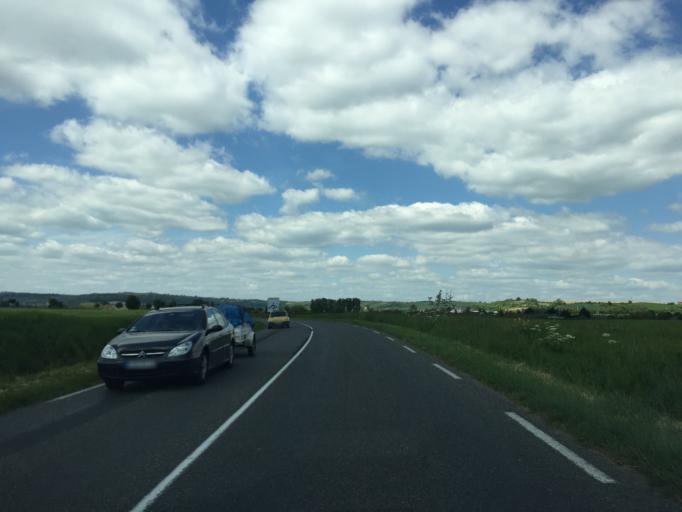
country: FR
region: Auvergne
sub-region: Departement du Puy-de-Dome
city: Aigueperse
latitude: 46.0228
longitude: 3.2232
